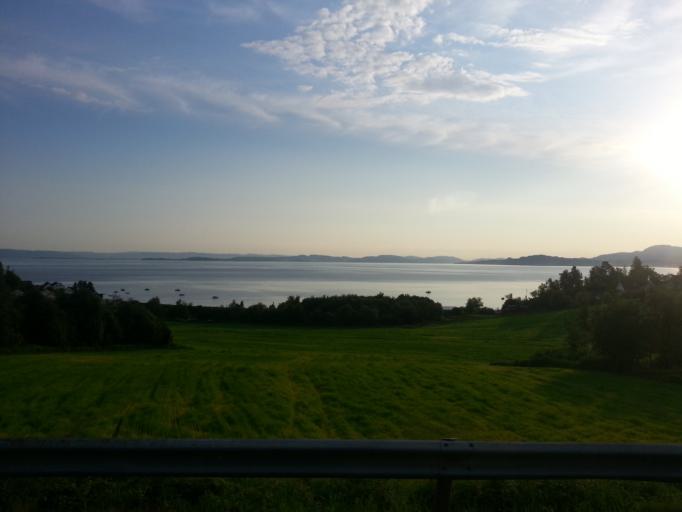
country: NO
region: Sor-Trondelag
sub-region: Malvik
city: Malvik
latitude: 63.4347
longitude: 10.6087
